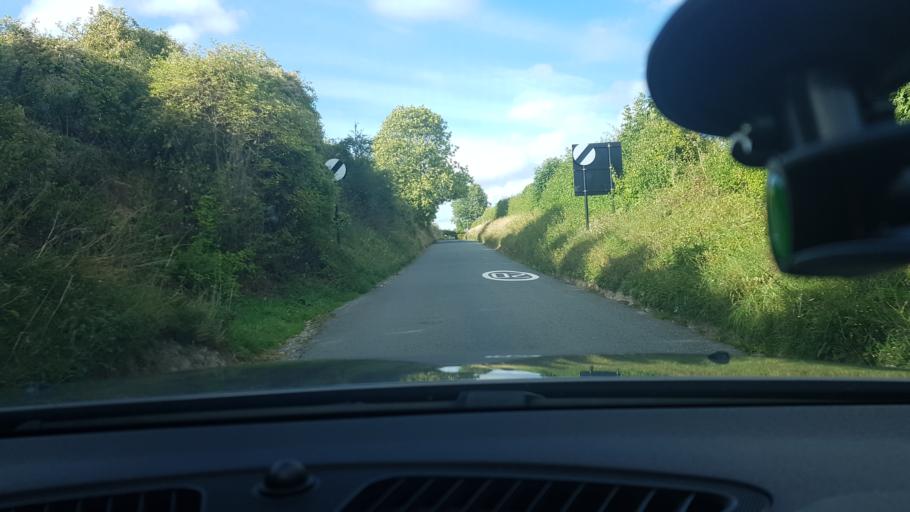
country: GB
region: England
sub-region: Wiltshire
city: Shalbourne
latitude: 51.3715
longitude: -1.5474
